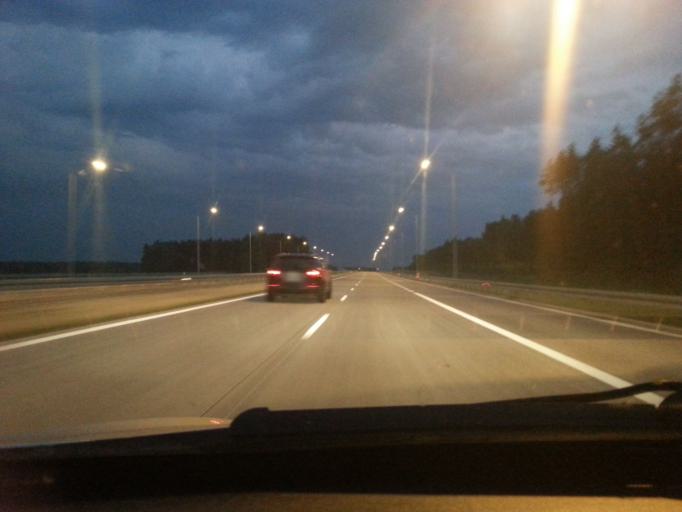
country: PL
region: Lodz Voivodeship
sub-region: Powiat sieradzki
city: Sieradz
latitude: 51.5252
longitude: 18.6950
